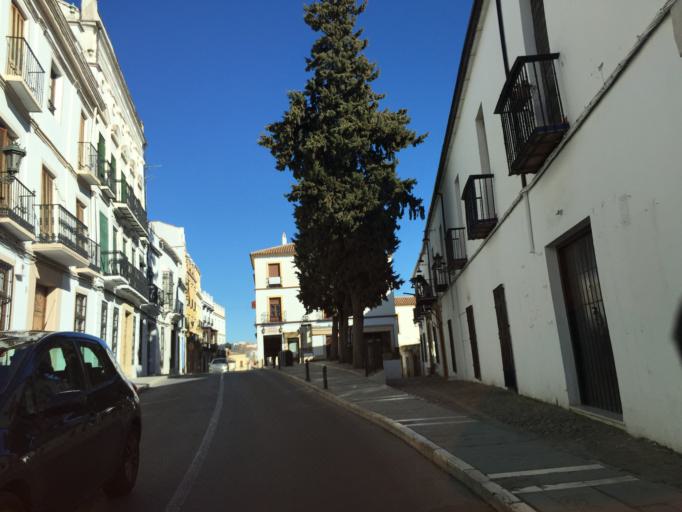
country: ES
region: Andalusia
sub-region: Provincia de Malaga
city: Ronda
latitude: 36.7390
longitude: -5.1651
